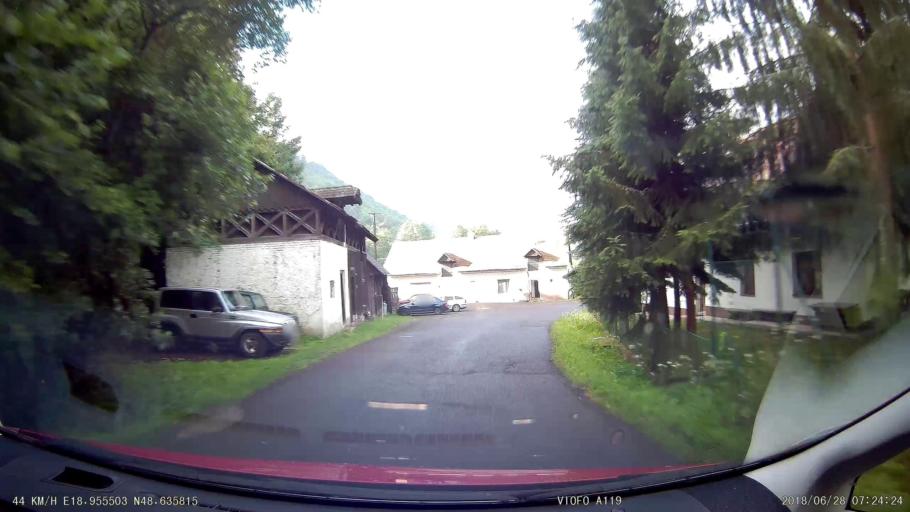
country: SK
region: Banskobystricky
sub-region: Okres Ziar nad Hronom
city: Kremnica
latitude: 48.6356
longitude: 18.9555
